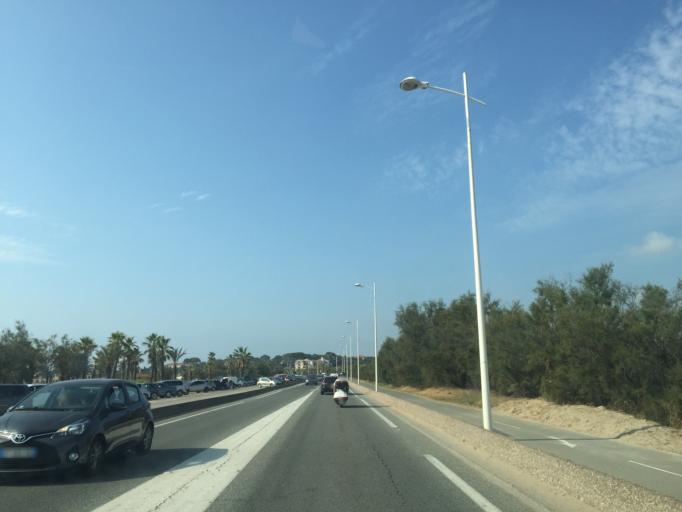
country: FR
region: Provence-Alpes-Cote d'Azur
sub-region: Departement du Var
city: Frejus
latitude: 43.3979
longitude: 6.7294
